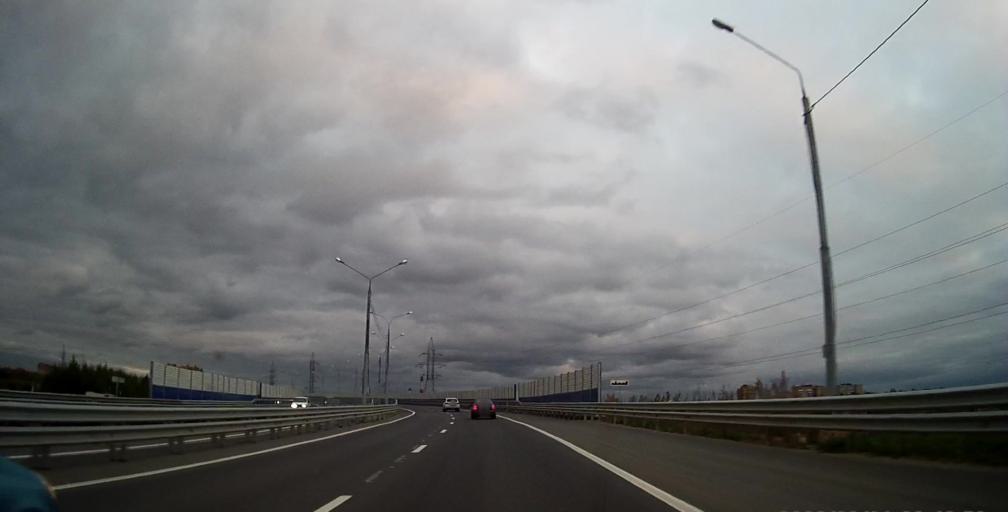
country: RU
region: Moskovskaya
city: Klimovsk
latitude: 55.3835
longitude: 37.5200
